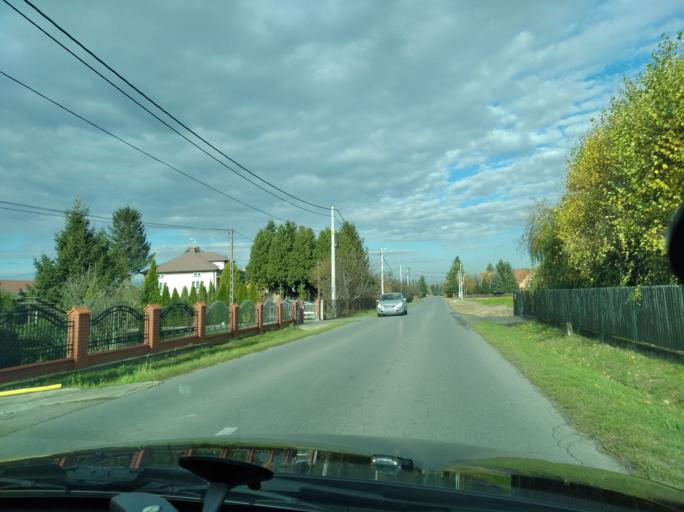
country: PL
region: Subcarpathian Voivodeship
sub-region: Powiat debicki
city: Brzeznica
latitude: 50.0729
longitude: 21.5271
